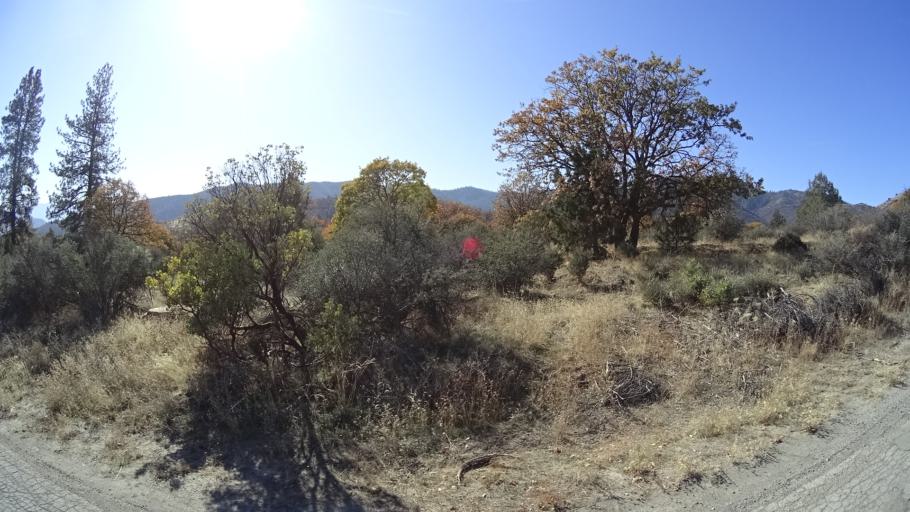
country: US
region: California
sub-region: Siskiyou County
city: Yreka
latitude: 41.7742
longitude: -122.6378
